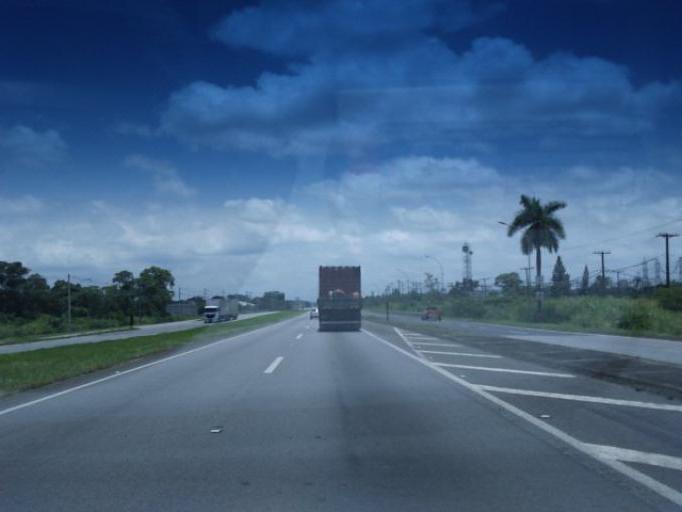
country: BR
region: Sao Paulo
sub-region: Registro
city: Registro
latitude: -24.5188
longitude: -47.8529
